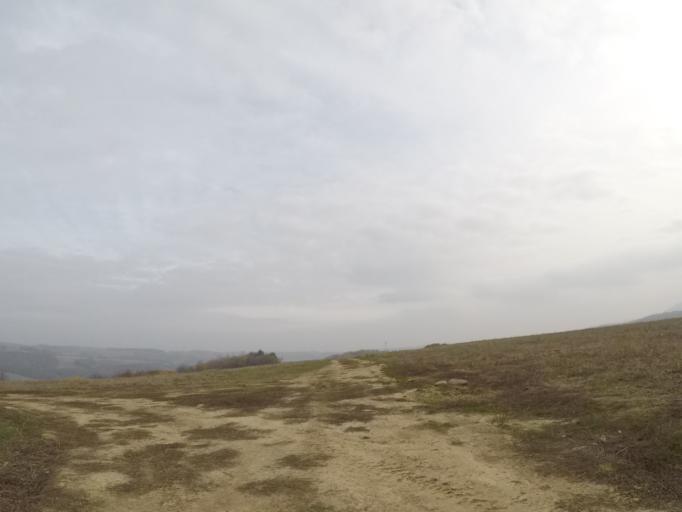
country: SK
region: Presovsky
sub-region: Okres Presov
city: Presov
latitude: 48.9393
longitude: 21.1584
